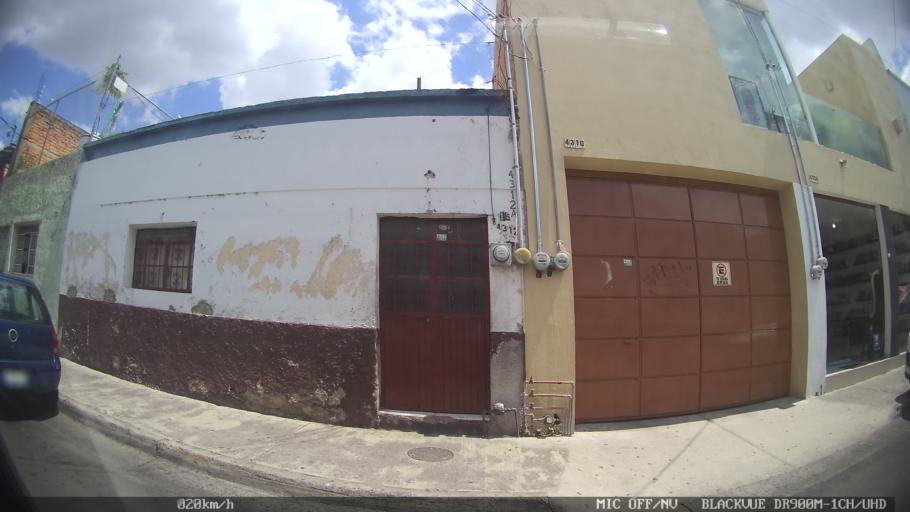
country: MX
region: Jalisco
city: Tlaquepaque
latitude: 20.6590
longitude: -103.2771
